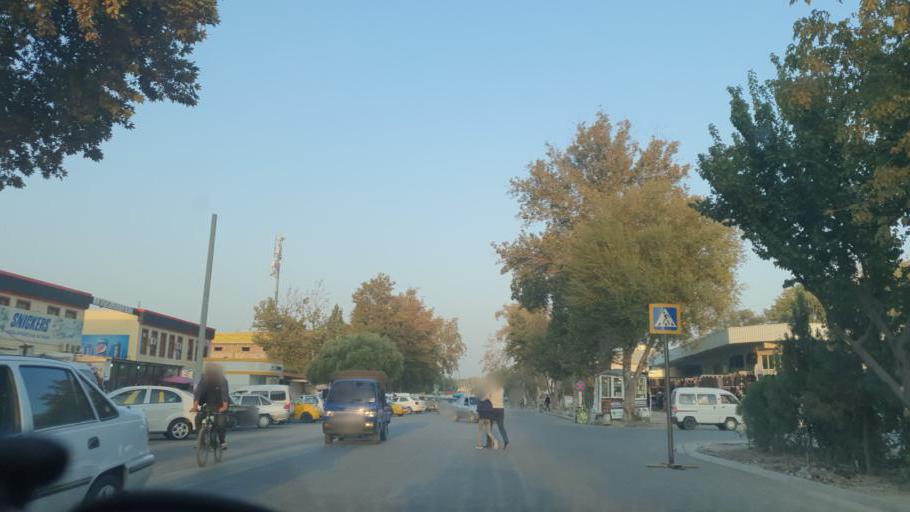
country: UZ
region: Fergana
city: Yaypan
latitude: 40.3807
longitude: 70.8098
